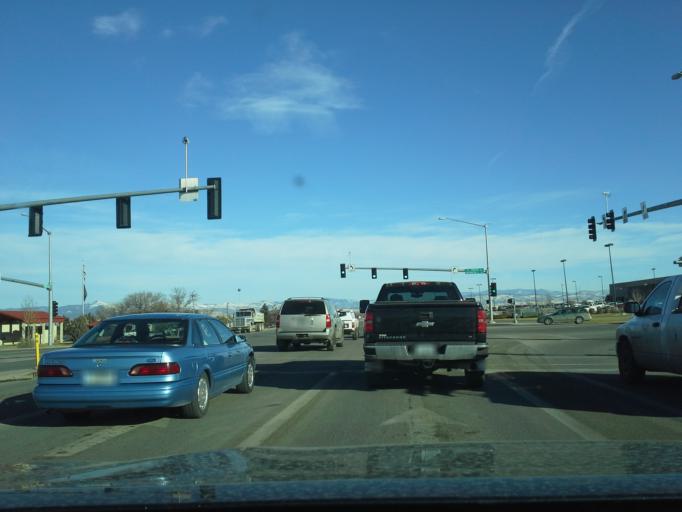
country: US
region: Montana
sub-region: Lewis and Clark County
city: Helena
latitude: 46.6166
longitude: -112.0070
